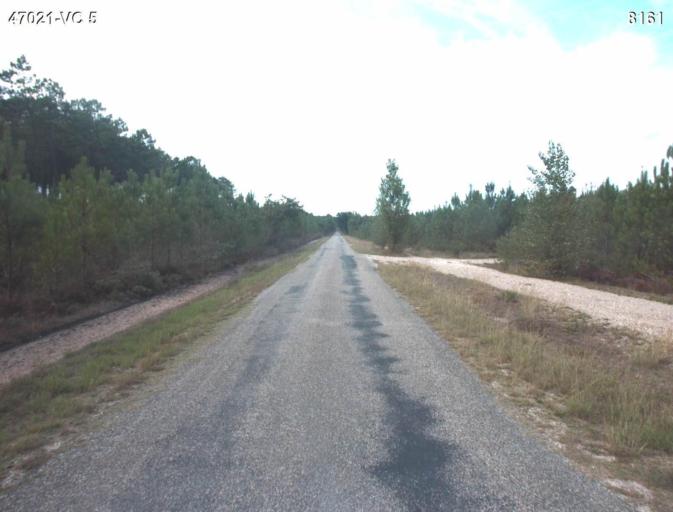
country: FR
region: Aquitaine
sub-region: Departement du Lot-et-Garonne
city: Barbaste
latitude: 44.1542
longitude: 0.2002
